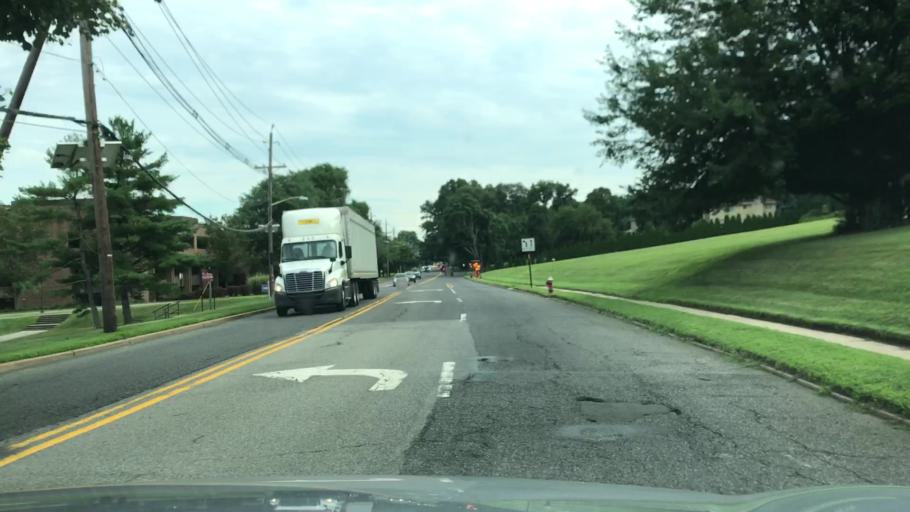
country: US
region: New Jersey
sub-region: Bergen County
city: Oradell
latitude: 40.9648
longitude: -74.0306
